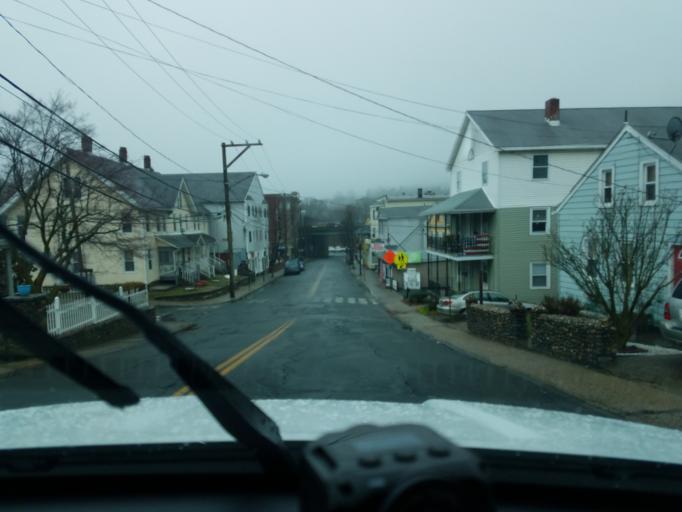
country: US
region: Connecticut
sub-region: New Haven County
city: Naugatuck
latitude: 41.4900
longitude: -73.0500
